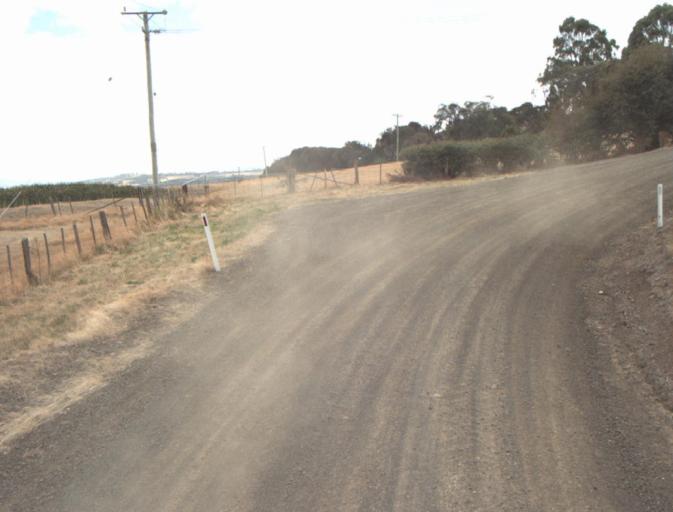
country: AU
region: Tasmania
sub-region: Northern Midlands
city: Evandale
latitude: -41.5141
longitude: 147.2919
